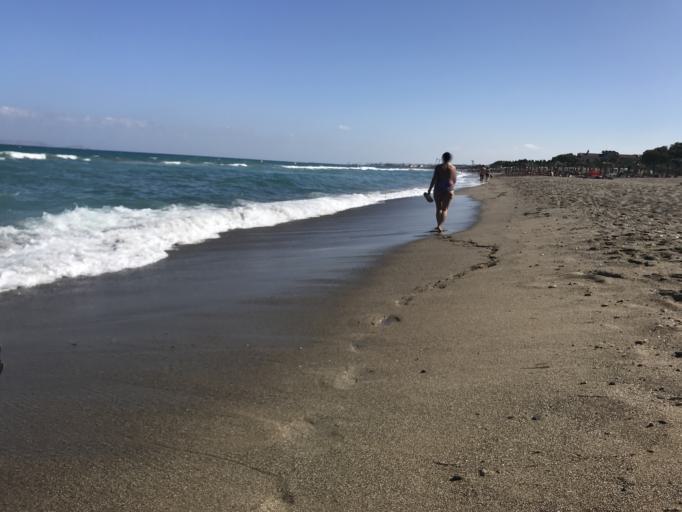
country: GR
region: Crete
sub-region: Nomos Irakleiou
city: Gazi
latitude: 35.3382
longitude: 25.0731
